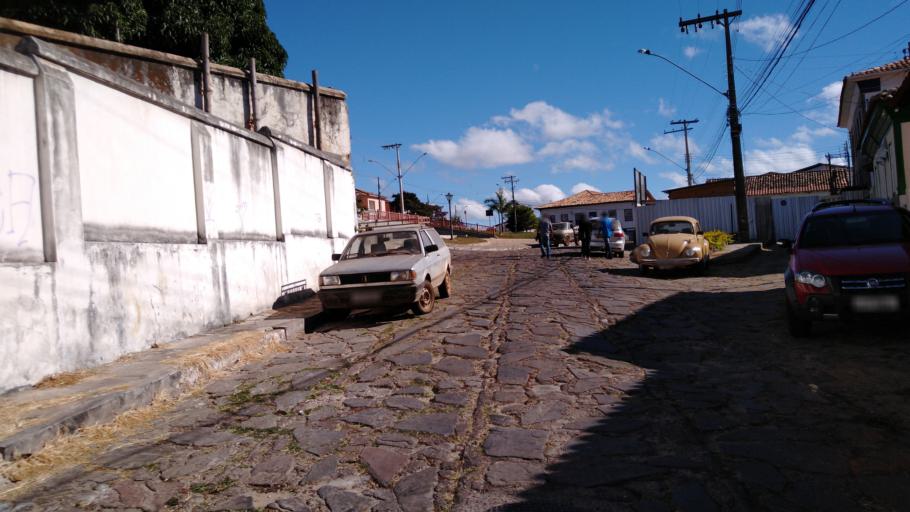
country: BR
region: Minas Gerais
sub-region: Diamantina
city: Diamantina
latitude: -18.2451
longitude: -43.5942
